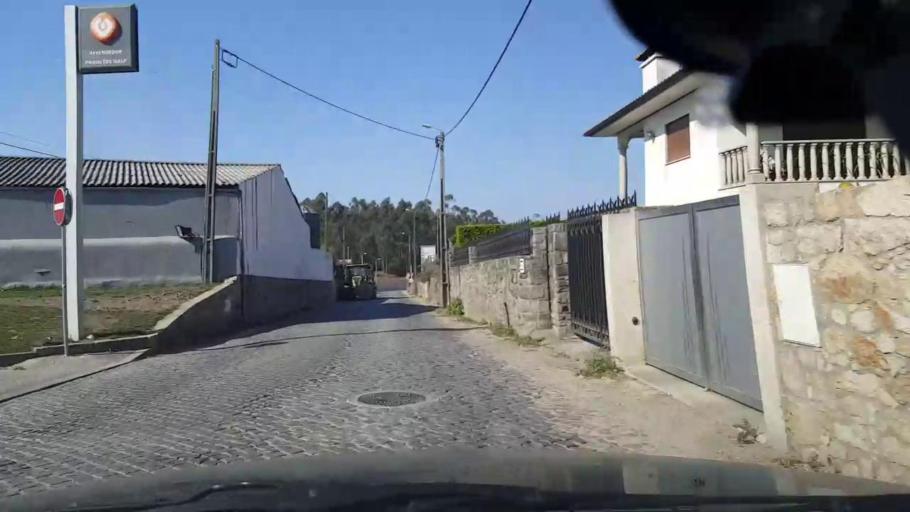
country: PT
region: Porto
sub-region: Vila do Conde
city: Arvore
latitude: 41.3854
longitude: -8.6859
